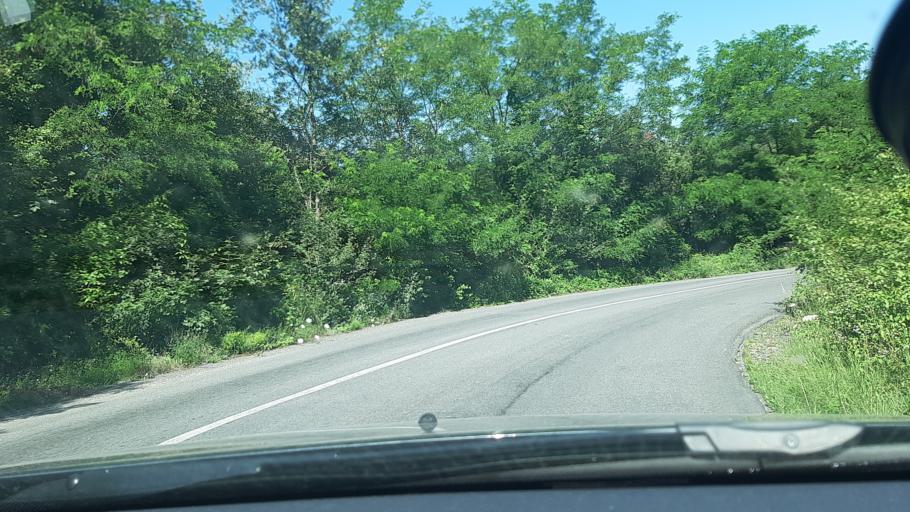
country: RO
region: Hunedoara
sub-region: Comuna Teliucu Inferior
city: Teliucu Inferior
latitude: 45.6977
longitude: 22.8778
